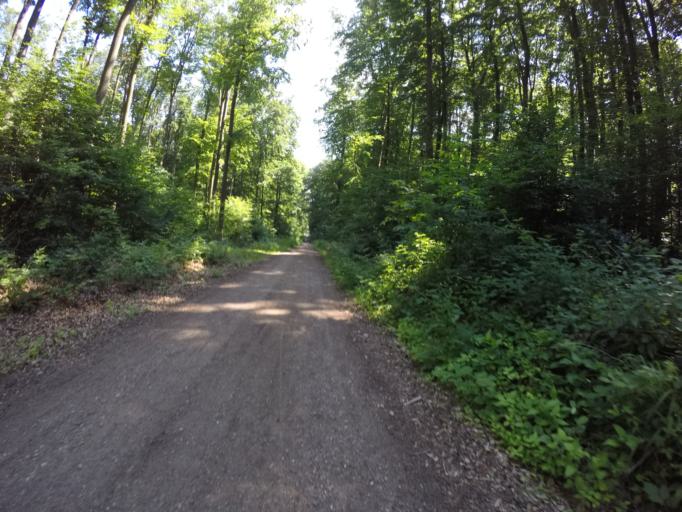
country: DE
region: Bavaria
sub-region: Lower Bavaria
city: Ihrlerstein
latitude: 48.9057
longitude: 11.8327
